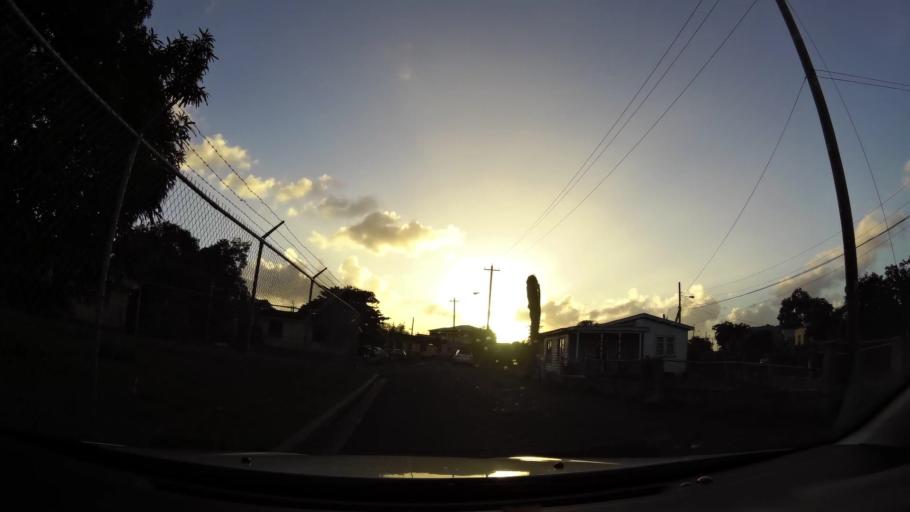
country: AG
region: Saint John
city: Saint John's
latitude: 17.1300
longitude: -61.8420
